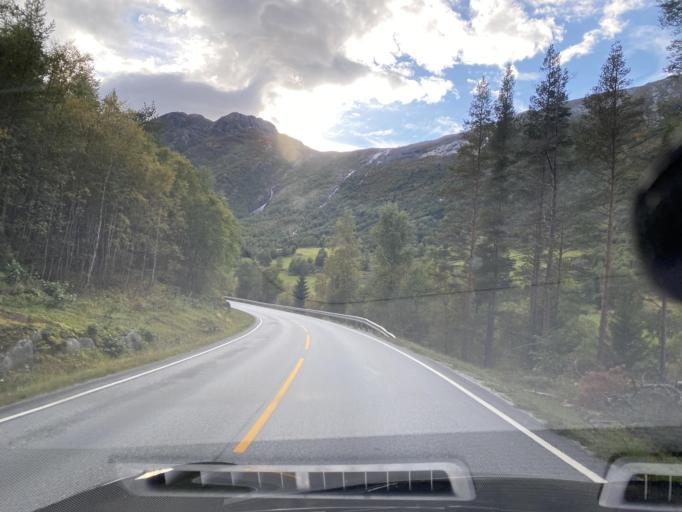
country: NO
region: Oppland
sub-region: Lom
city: Fossbergom
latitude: 61.8083
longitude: 8.4630
